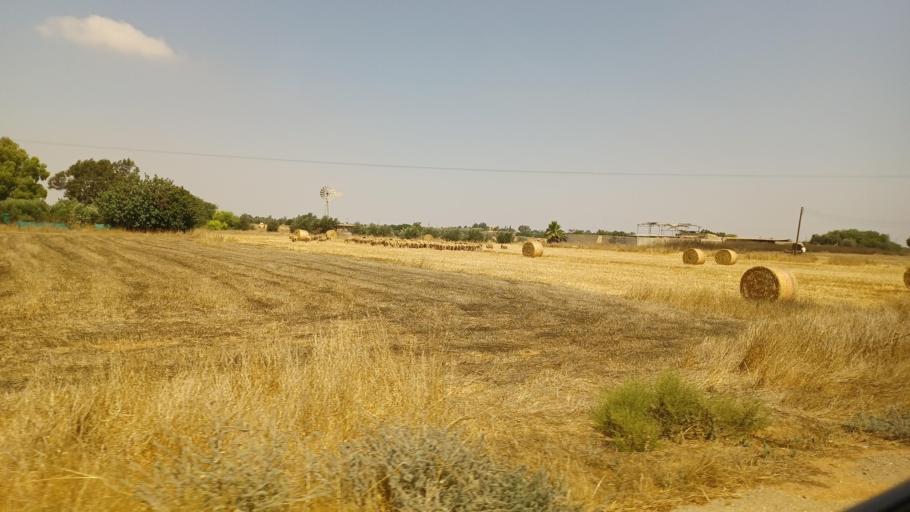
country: CY
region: Ammochostos
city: Frenaros
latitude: 35.0551
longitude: 33.9218
